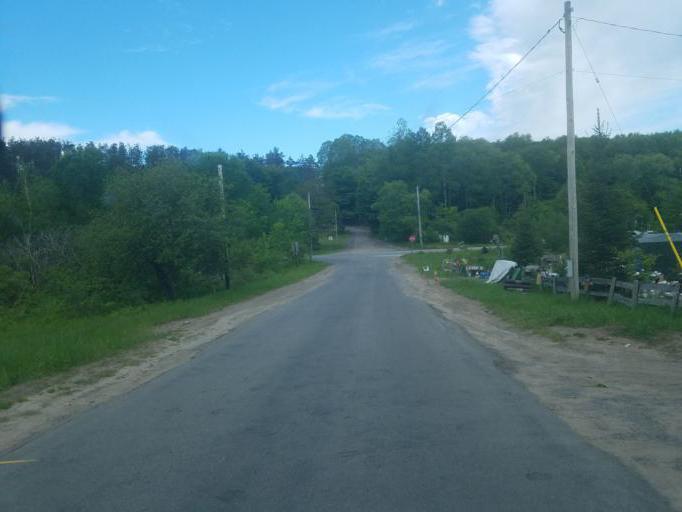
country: US
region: New York
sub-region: Herkimer County
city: Herkimer
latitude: 43.2610
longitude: -74.9896
